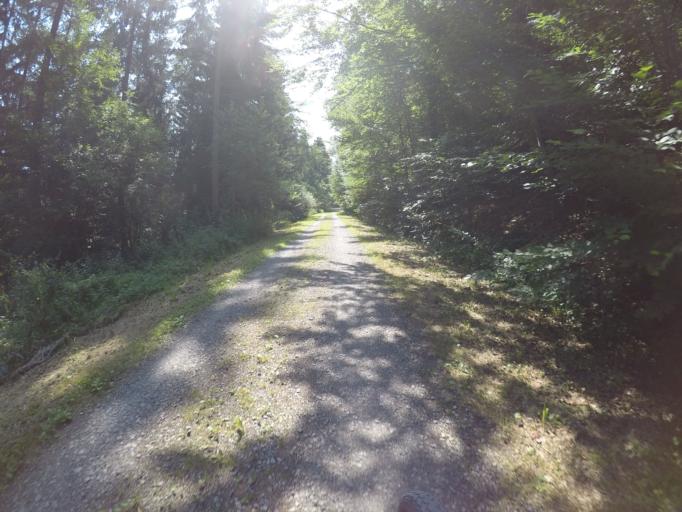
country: DE
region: Baden-Wuerttemberg
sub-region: Regierungsbezirk Stuttgart
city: Schlaitdorf
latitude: 48.6268
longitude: 9.1935
